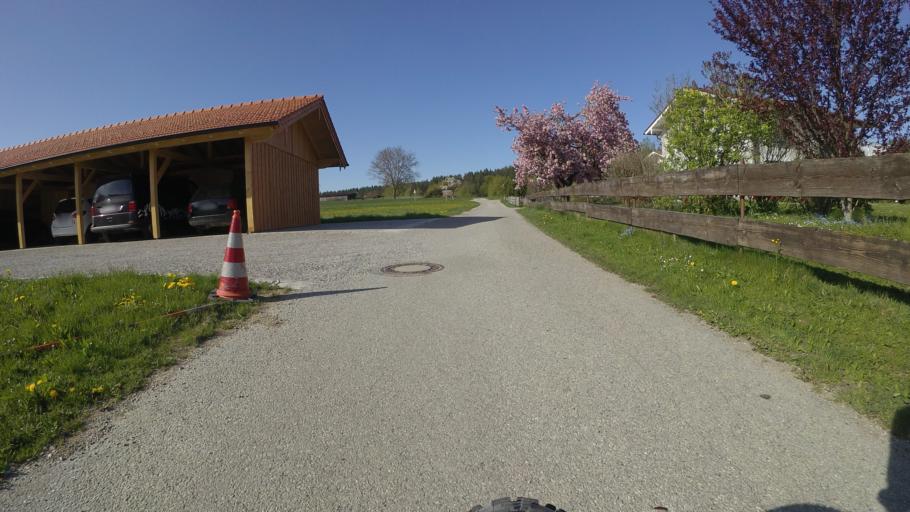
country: DE
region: Bavaria
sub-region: Upper Bavaria
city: Grabenstatt
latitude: 47.8535
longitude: 12.5614
